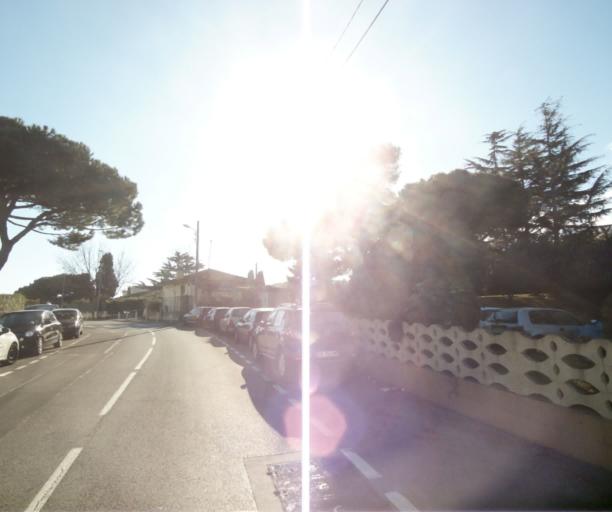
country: FR
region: Provence-Alpes-Cote d'Azur
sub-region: Departement des Alpes-Maritimes
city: Biot
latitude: 43.6067
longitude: 7.1211
